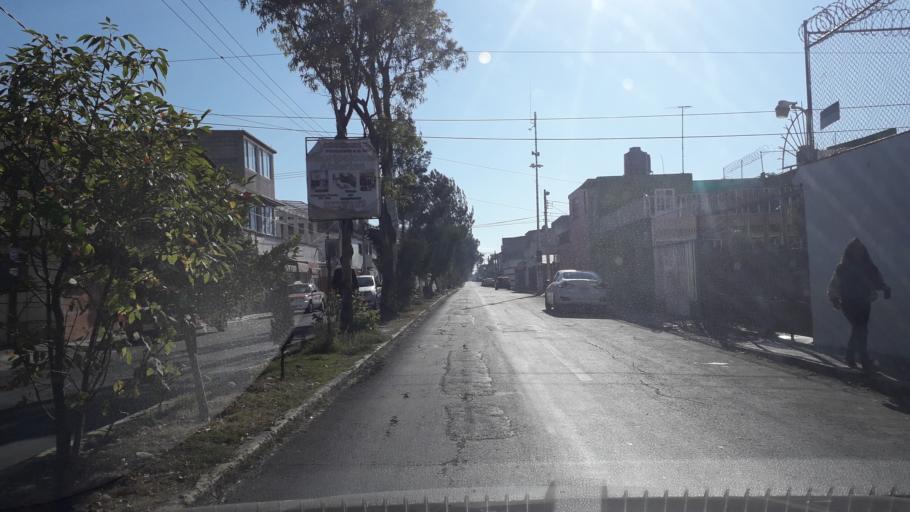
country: MX
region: Mexico City
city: Gustavo A. Madero
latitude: 19.5085
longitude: -99.0849
